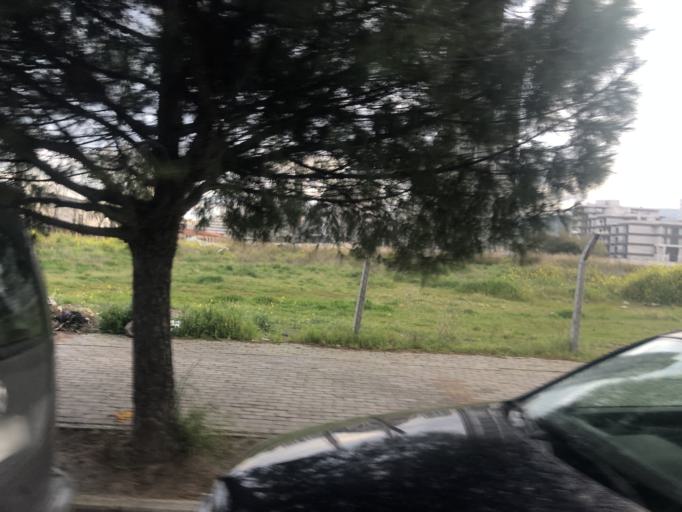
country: TR
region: Izmir
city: Karsiyaka
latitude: 38.4723
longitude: 27.0687
